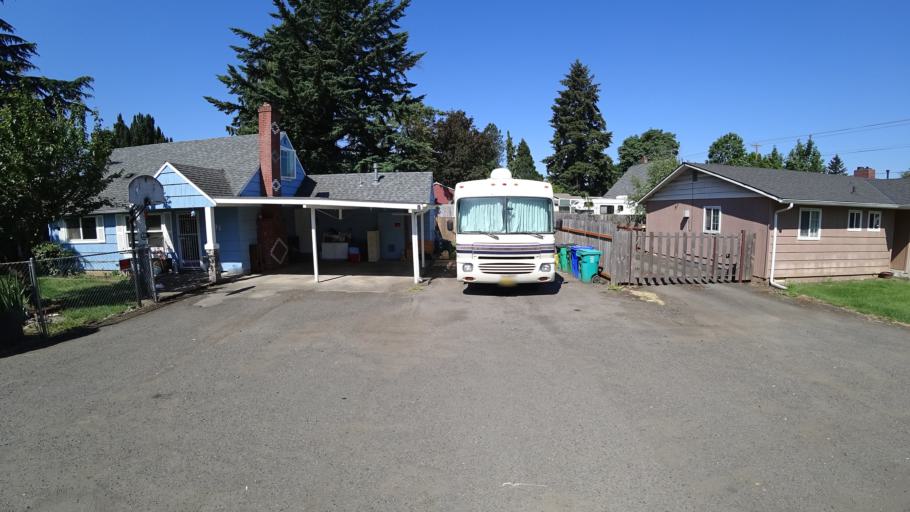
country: US
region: Oregon
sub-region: Multnomah County
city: Lents
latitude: 45.4824
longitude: -122.5491
